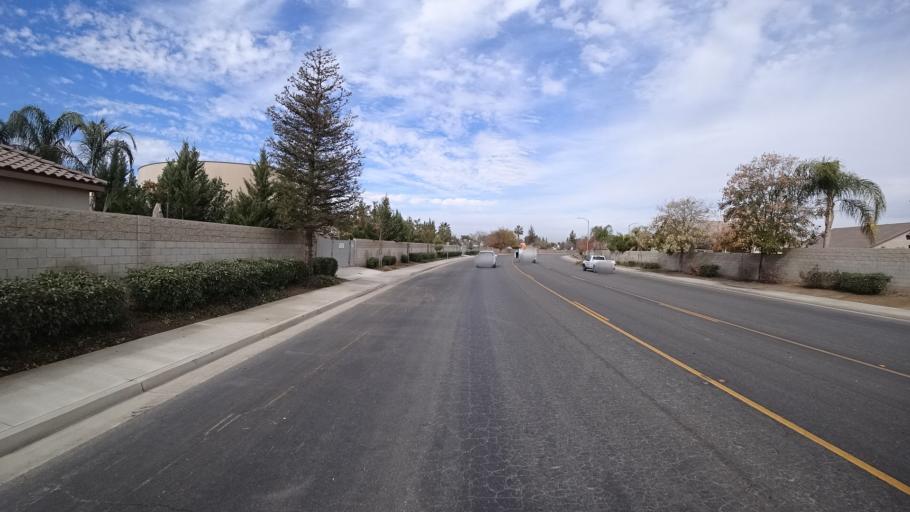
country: US
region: California
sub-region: Kern County
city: Rosedale
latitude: 35.3929
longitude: -119.1362
